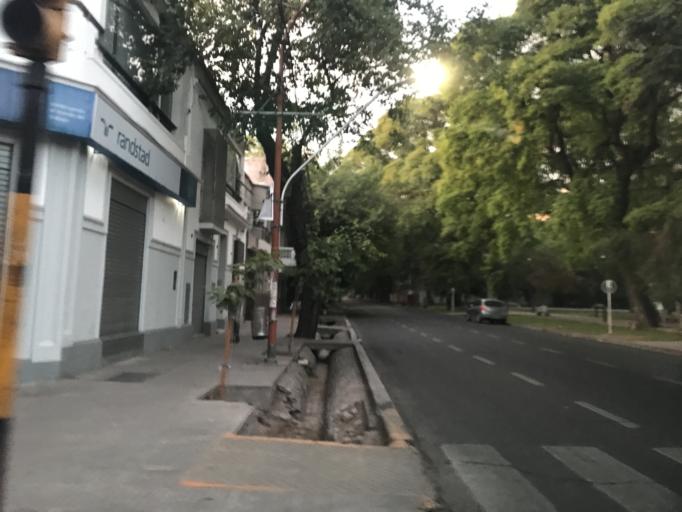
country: AR
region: Mendoza
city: Mendoza
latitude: -32.8860
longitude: -68.8462
